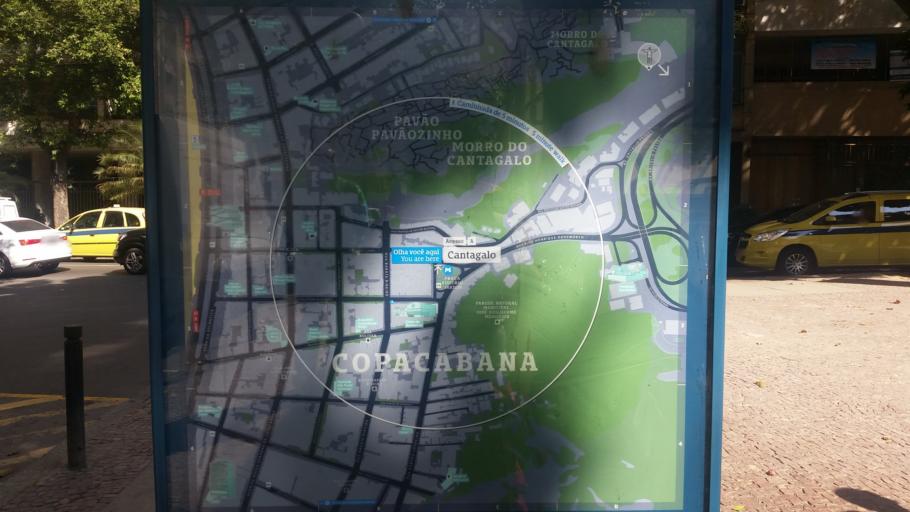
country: BR
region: Rio de Janeiro
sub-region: Rio De Janeiro
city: Rio de Janeiro
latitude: -22.9768
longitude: -43.1939
